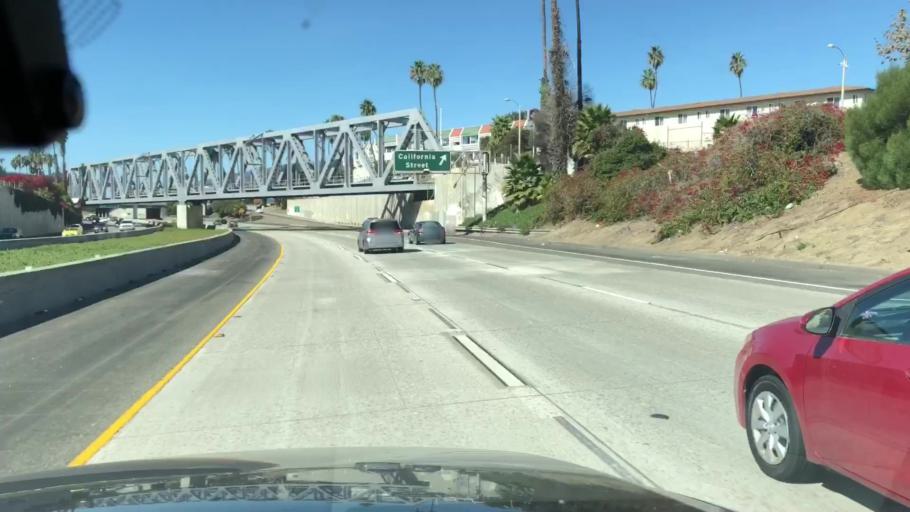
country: US
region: California
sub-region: Ventura County
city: Ventura
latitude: 34.2765
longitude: -119.2892
